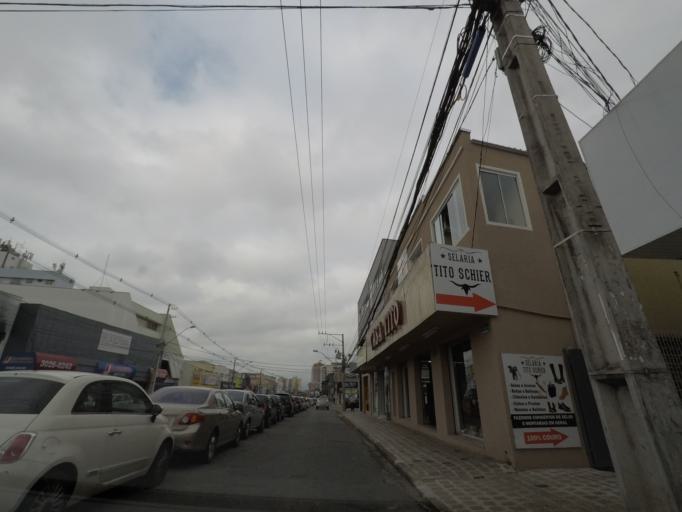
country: BR
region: Parana
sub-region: Curitiba
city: Curitiba
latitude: -25.4825
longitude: -49.2931
